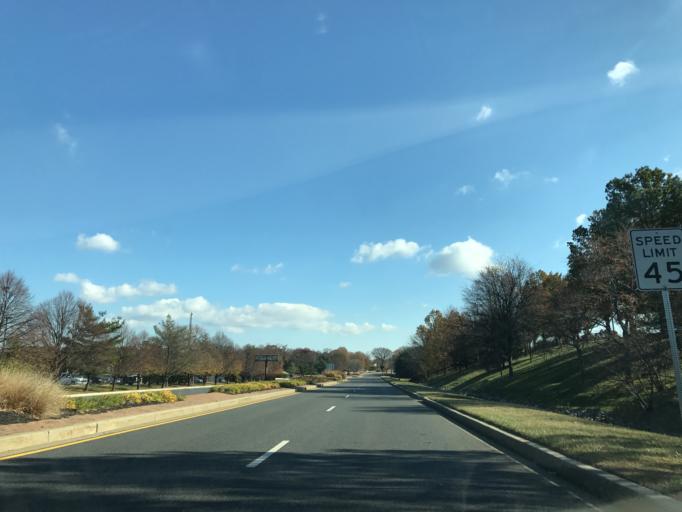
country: US
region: Maryland
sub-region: Anne Arundel County
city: Linthicum
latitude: 39.1900
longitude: -76.6589
